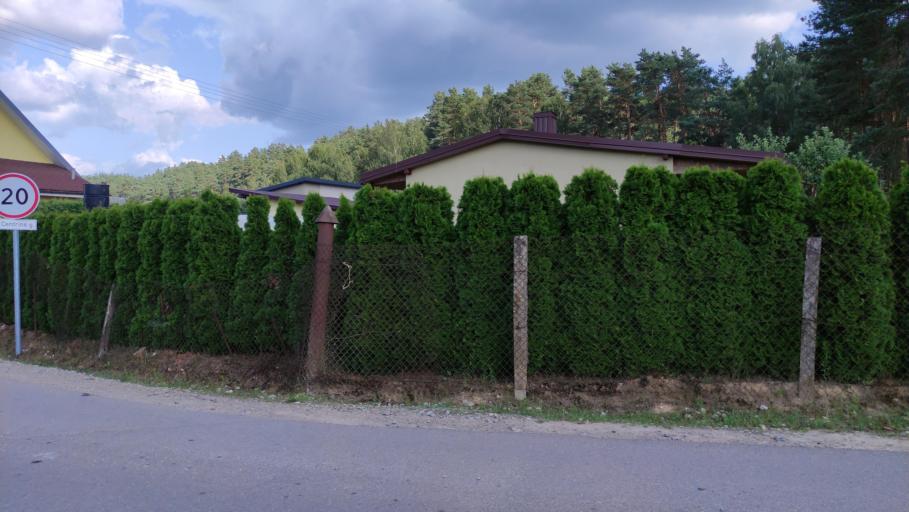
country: LT
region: Alytaus apskritis
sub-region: Alytus
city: Alytus
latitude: 54.4291
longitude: 24.0637
